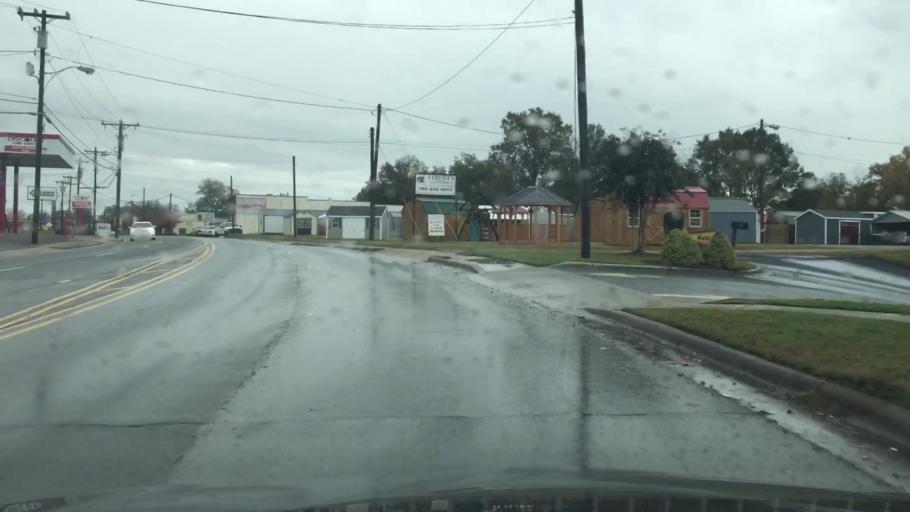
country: US
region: North Carolina
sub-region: Rowan County
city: Salisbury
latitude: 35.6748
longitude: -80.4794
